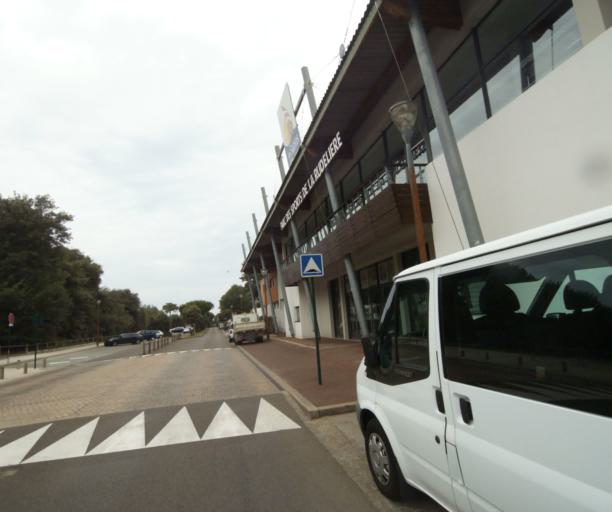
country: FR
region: Pays de la Loire
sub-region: Departement de la Vendee
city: Chateau-d'Olonne
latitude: 46.4853
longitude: -1.7567
